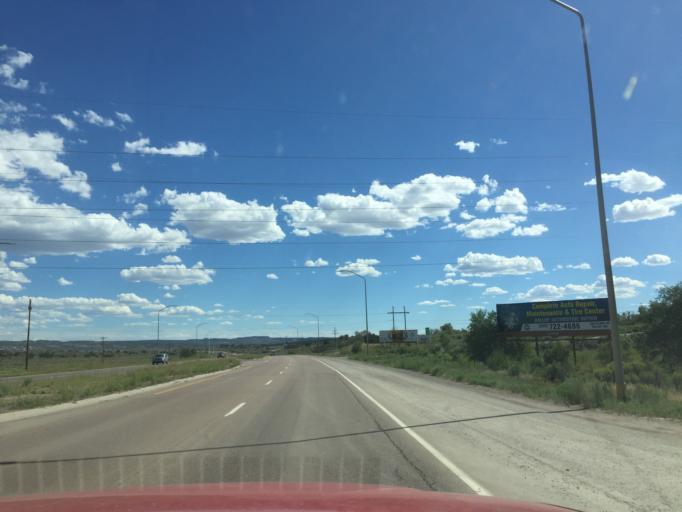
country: US
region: New Mexico
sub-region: McKinley County
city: Gallup
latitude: 35.5710
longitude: -108.7593
